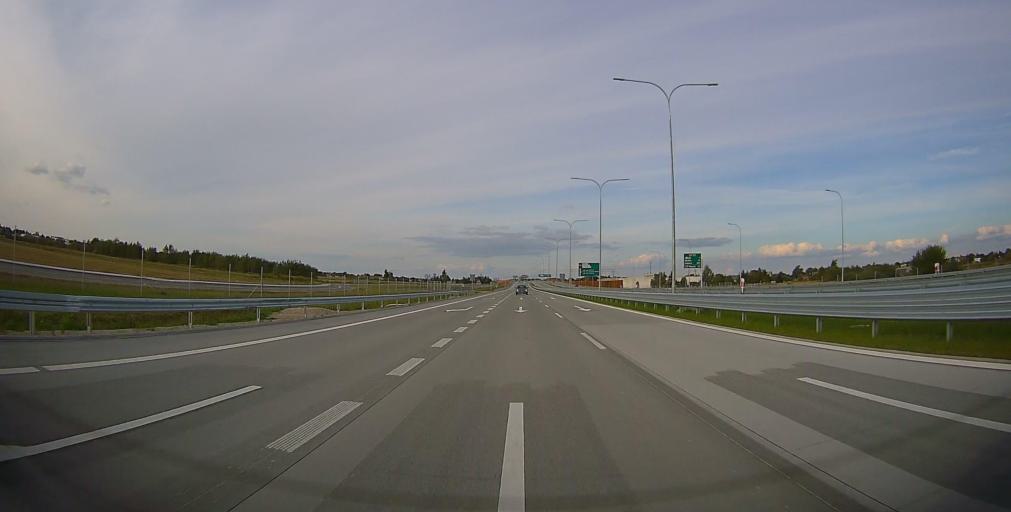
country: PL
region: Masovian Voivodeship
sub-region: Powiat piaseczynski
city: Mysiadlo
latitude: 52.1219
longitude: 20.9881
